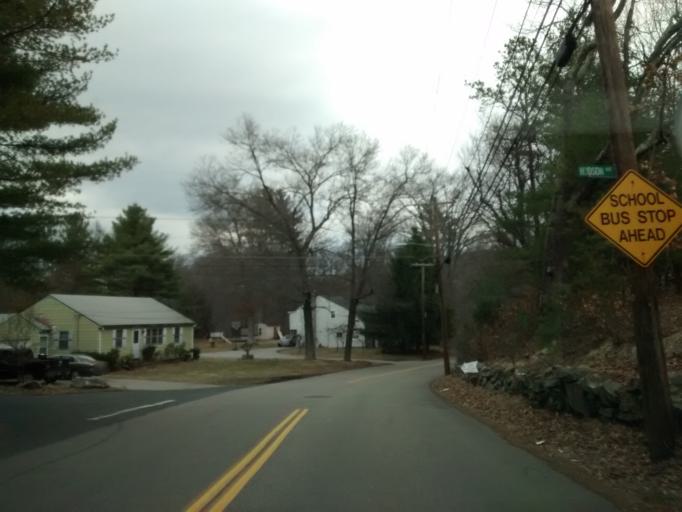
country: US
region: Massachusetts
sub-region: Worcester County
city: Grafton
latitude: 42.1981
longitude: -71.6954
